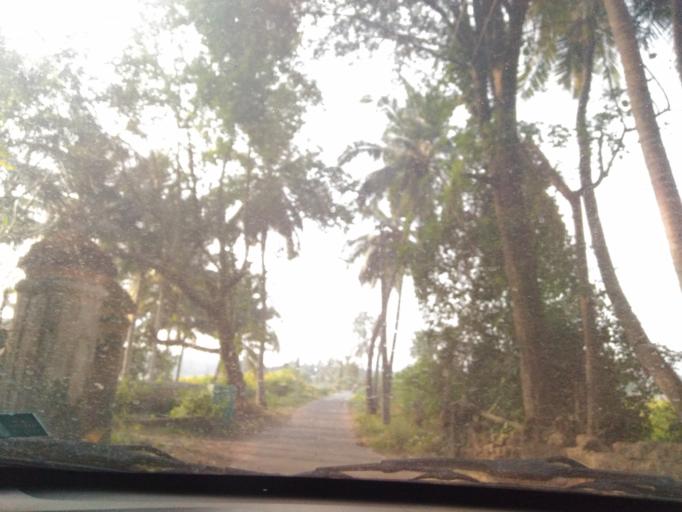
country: IN
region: Goa
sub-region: South Goa
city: Cuncolim
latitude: 15.1762
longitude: 73.9706
